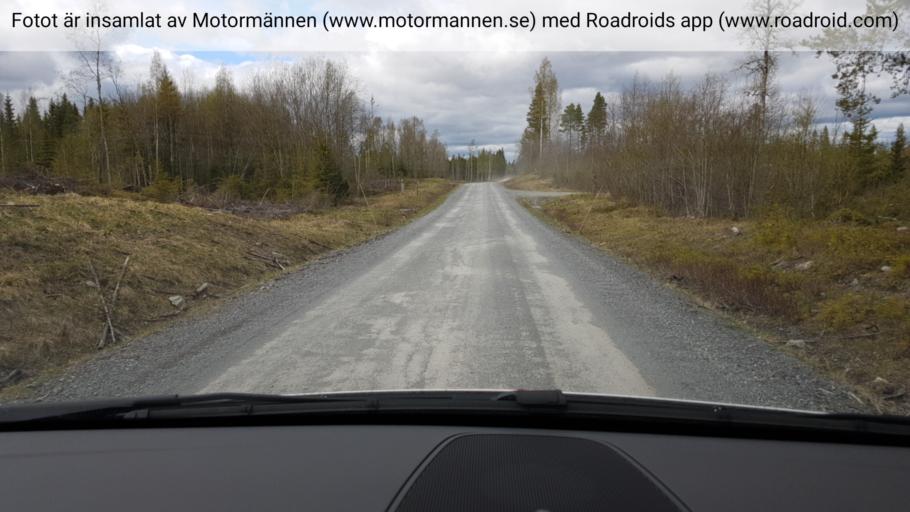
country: SE
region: Jaemtland
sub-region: OEstersunds Kommun
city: Brunflo
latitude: 63.1354
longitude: 15.0692
